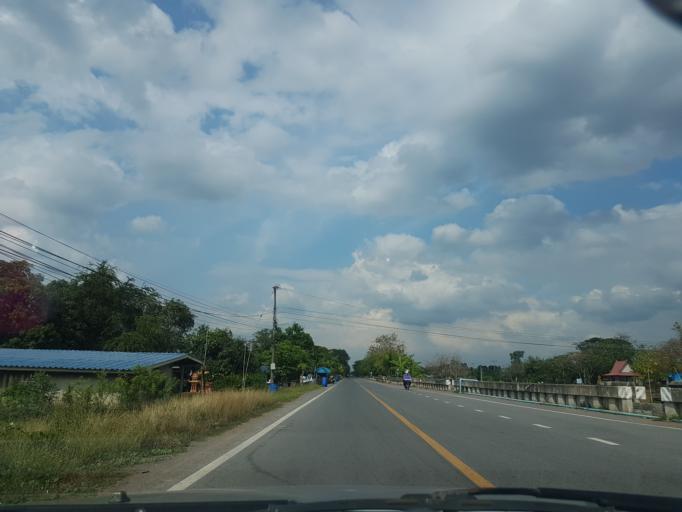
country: TH
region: Pathum Thani
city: Nong Suea
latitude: 14.1774
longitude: 100.8915
